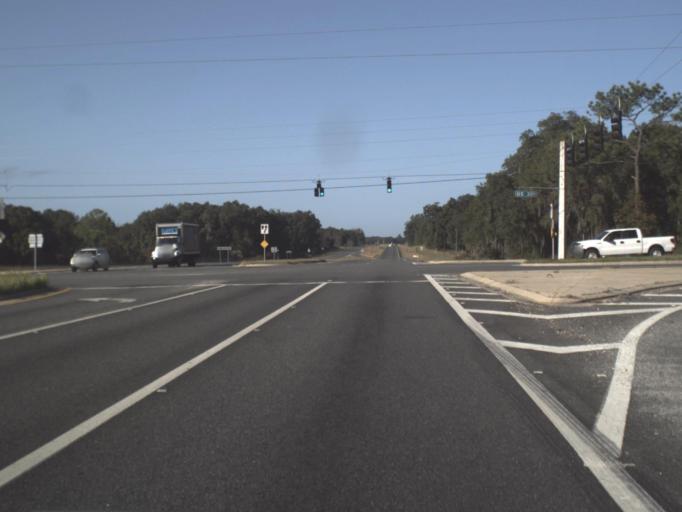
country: US
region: Florida
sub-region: Marion County
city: Belleview
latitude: 29.0294
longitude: -82.0444
